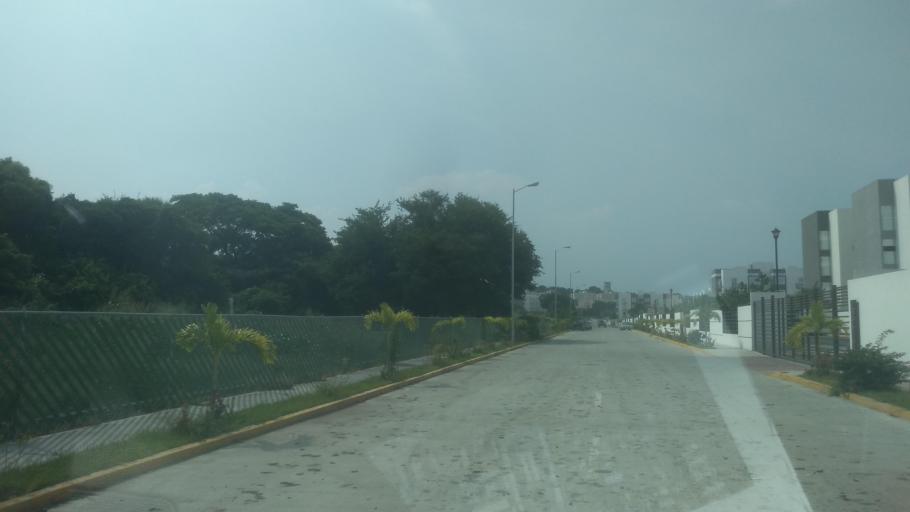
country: MX
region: Veracruz
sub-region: Veracruz
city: Lomas de Rio Medio Cuatro
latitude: 19.1765
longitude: -96.2061
